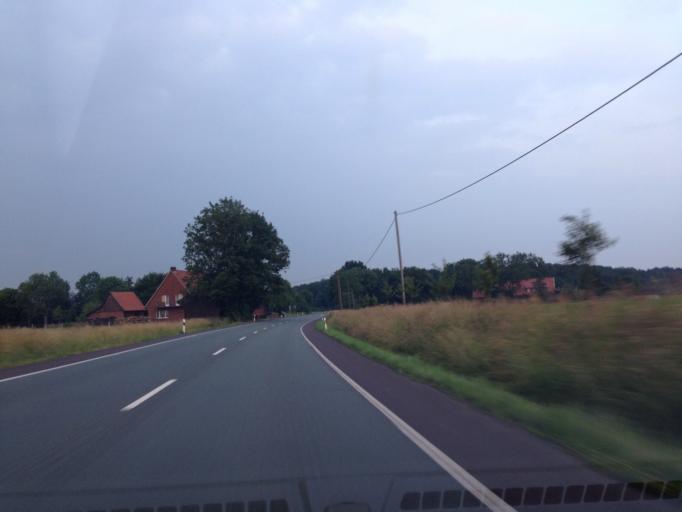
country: DE
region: North Rhine-Westphalia
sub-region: Regierungsbezirk Munster
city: Senden
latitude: 51.8780
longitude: 7.4568
